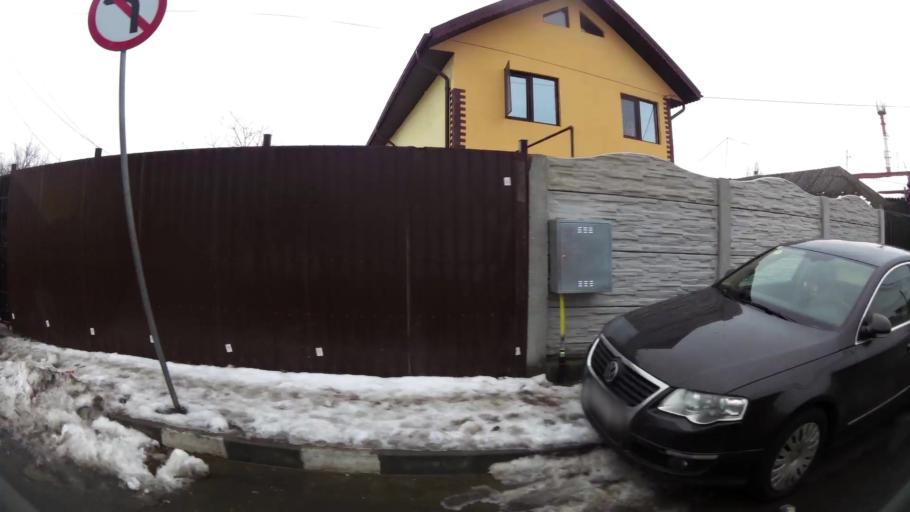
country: RO
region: Ilfov
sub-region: Comuna Pantelimon
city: Pantelimon
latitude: 44.4598
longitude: 26.2049
